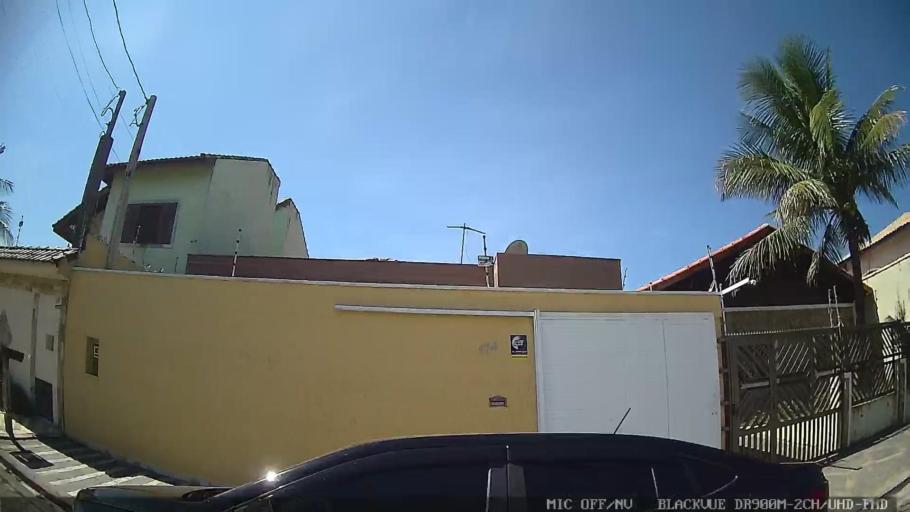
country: BR
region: Sao Paulo
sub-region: Peruibe
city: Peruibe
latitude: -24.2998
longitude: -46.9703
